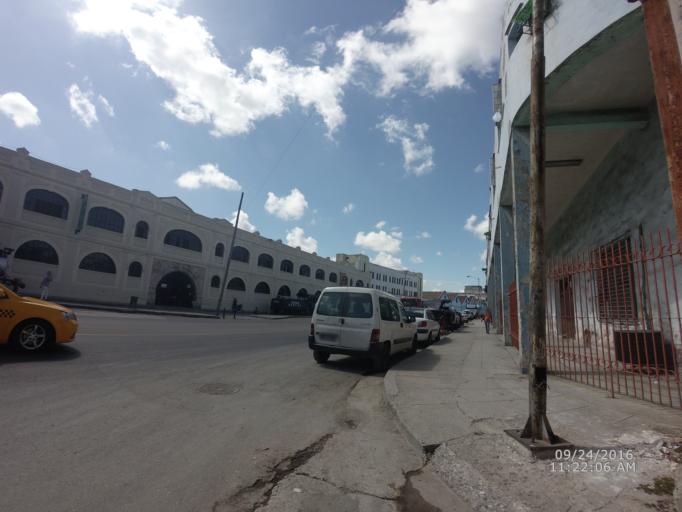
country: CU
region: La Habana
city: La Habana Vieja
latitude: 23.1302
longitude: -82.3496
